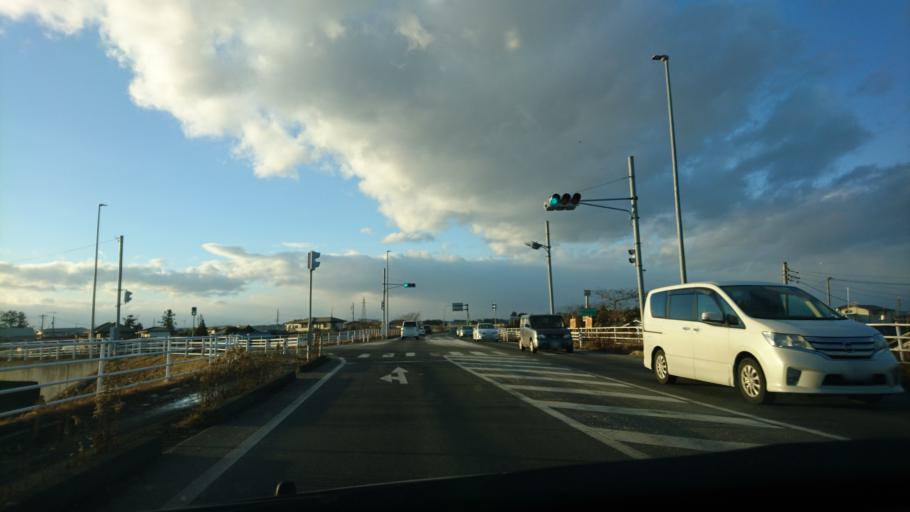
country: JP
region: Miyagi
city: Wakuya
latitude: 38.7227
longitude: 141.1515
